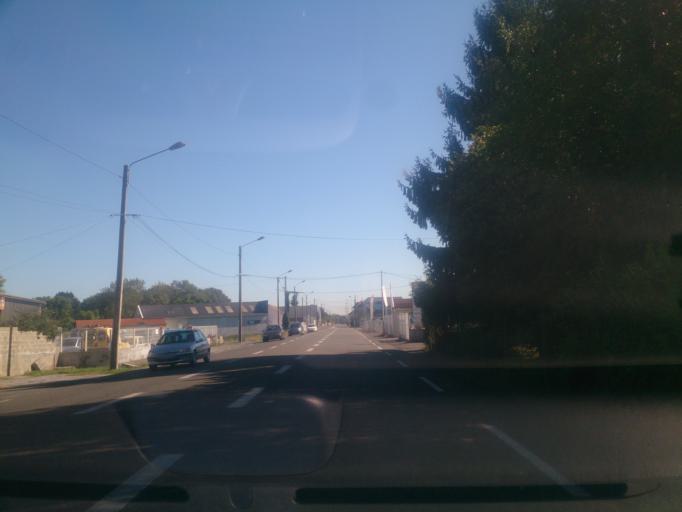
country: FR
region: Midi-Pyrenees
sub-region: Departement des Hautes-Pyrenees
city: Juillan
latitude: 43.1948
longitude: 0.0280
